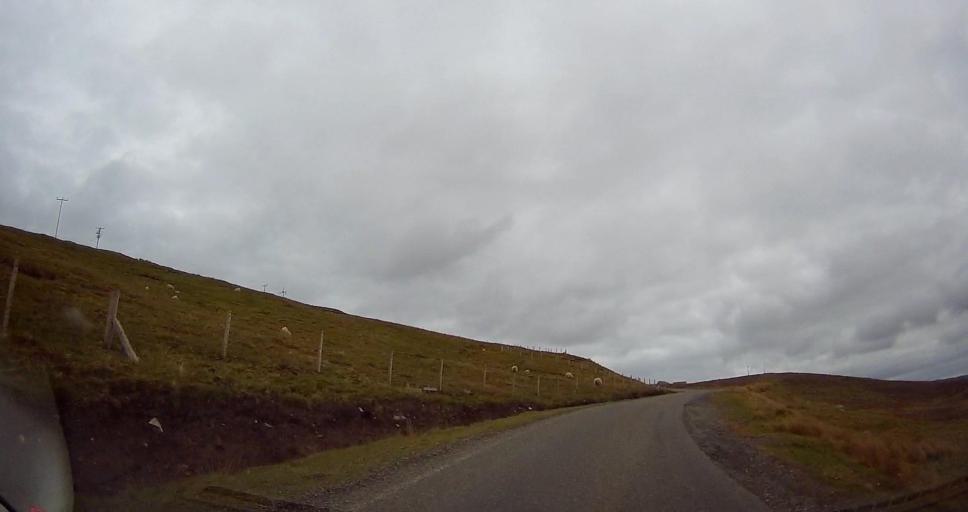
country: GB
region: Scotland
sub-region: Shetland Islands
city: Shetland
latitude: 60.6023
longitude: -1.0812
